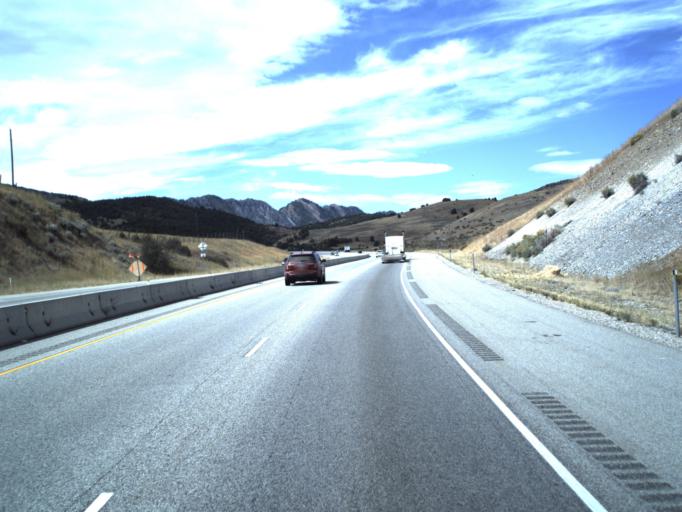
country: US
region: Utah
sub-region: Box Elder County
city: Brigham City
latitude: 41.5229
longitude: -111.9458
